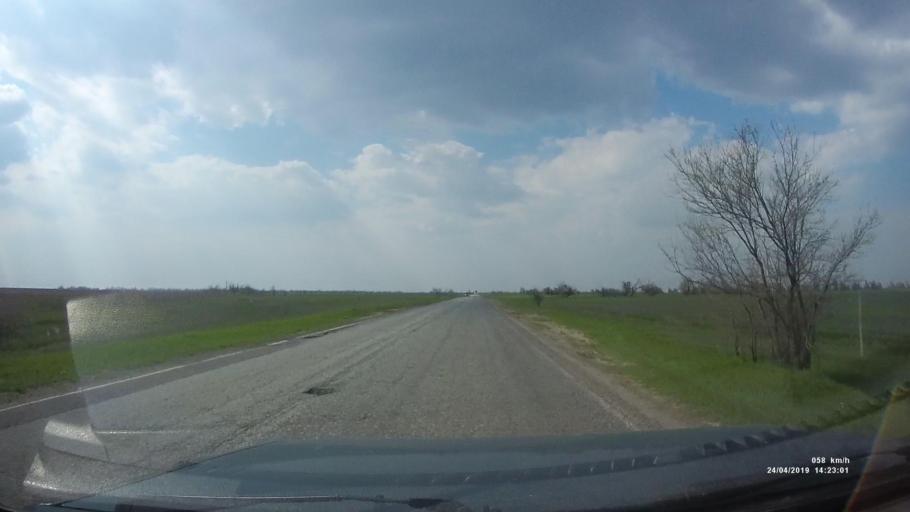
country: RU
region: Kalmykiya
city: Arshan'
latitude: 46.3188
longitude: 44.1196
